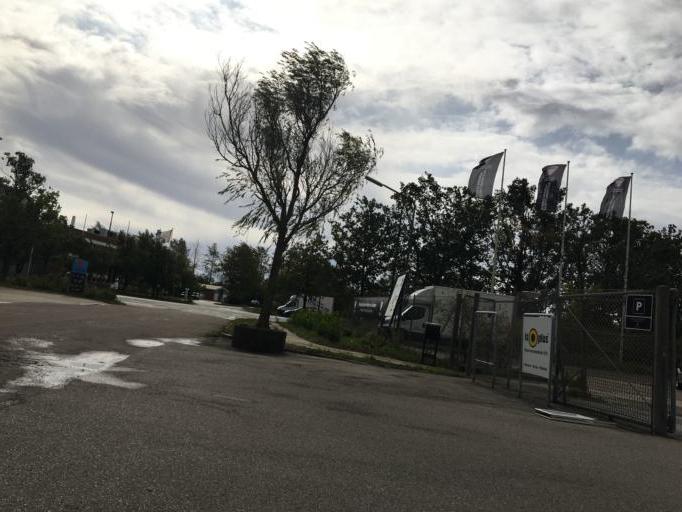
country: DK
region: Capital Region
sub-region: Hvidovre Kommune
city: Hvidovre
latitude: 55.6144
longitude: 12.4648
